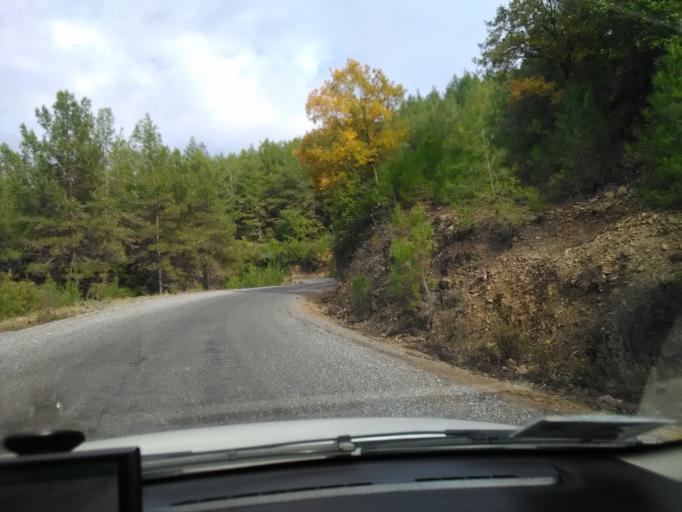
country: TR
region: Antalya
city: Gazipasa
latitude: 36.2467
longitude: 32.4212
